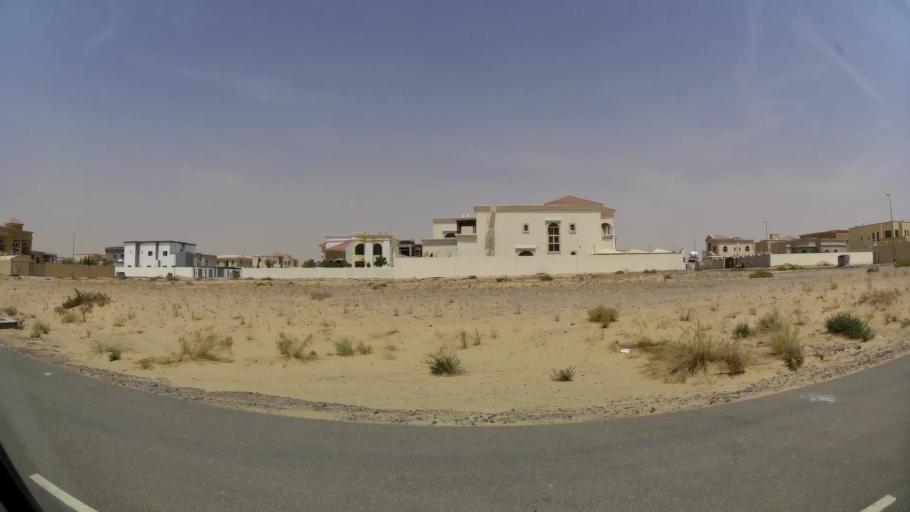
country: AE
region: Ash Shariqah
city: Sharjah
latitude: 25.2463
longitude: 55.5048
